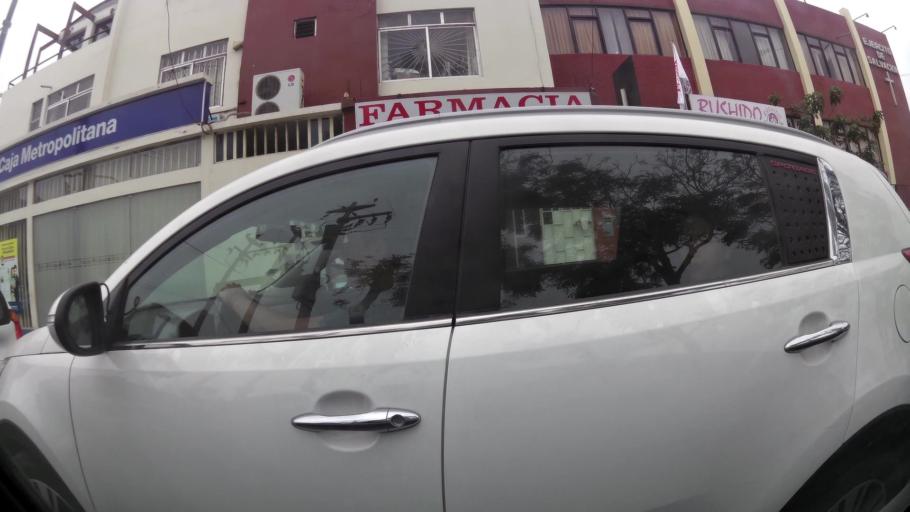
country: PE
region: La Libertad
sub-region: Provincia de Trujillo
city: Trujillo
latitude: -8.1164
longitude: -79.0262
